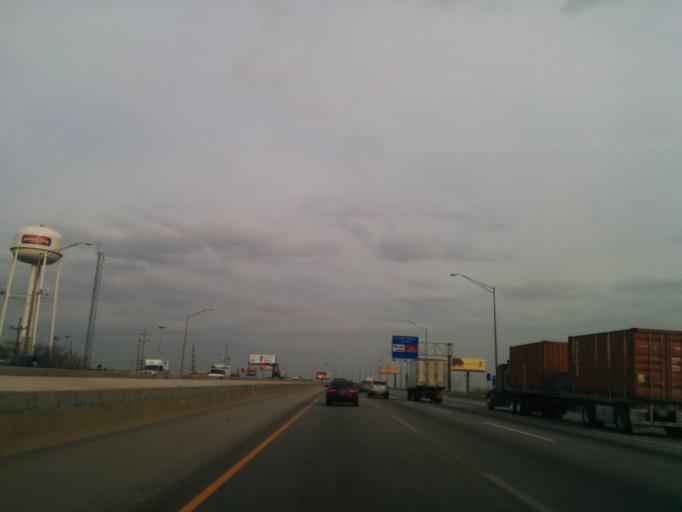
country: US
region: Illinois
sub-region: Cook County
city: Northlake
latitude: 41.9400
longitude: -87.8972
